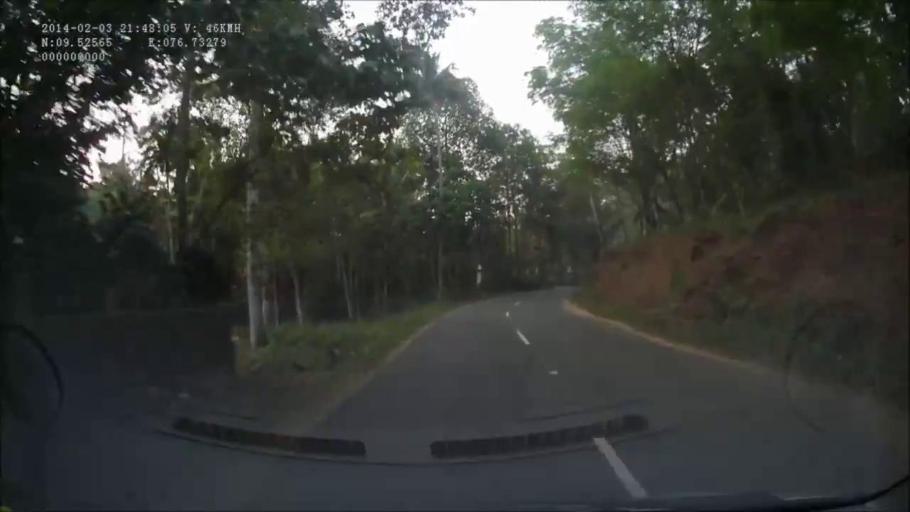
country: IN
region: Kerala
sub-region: Kottayam
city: Erattupetta
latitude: 9.5267
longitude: 76.7323
